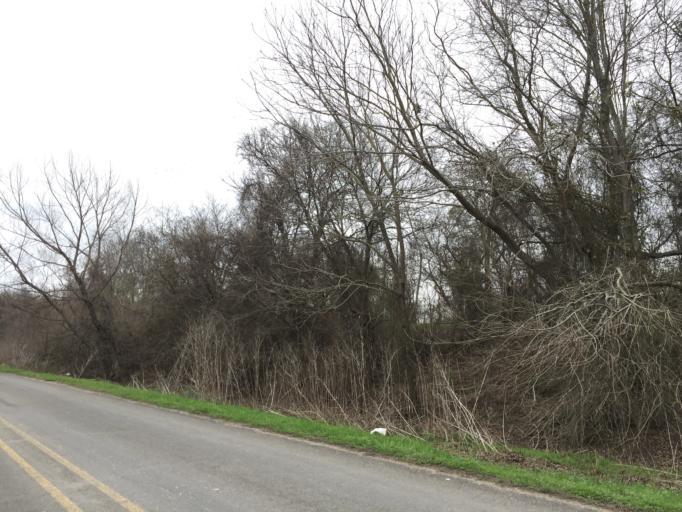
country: US
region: Texas
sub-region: Bell County
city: Belton
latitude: 31.0453
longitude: -97.4196
